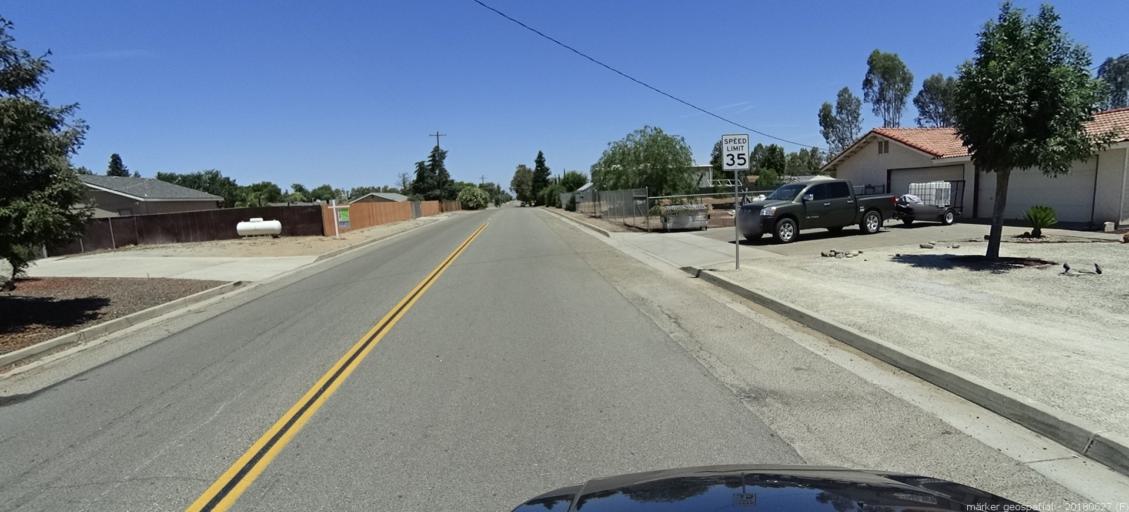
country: US
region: California
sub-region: Madera County
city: Bonadelle Ranchos-Madera Ranchos
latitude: 36.9232
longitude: -119.8625
